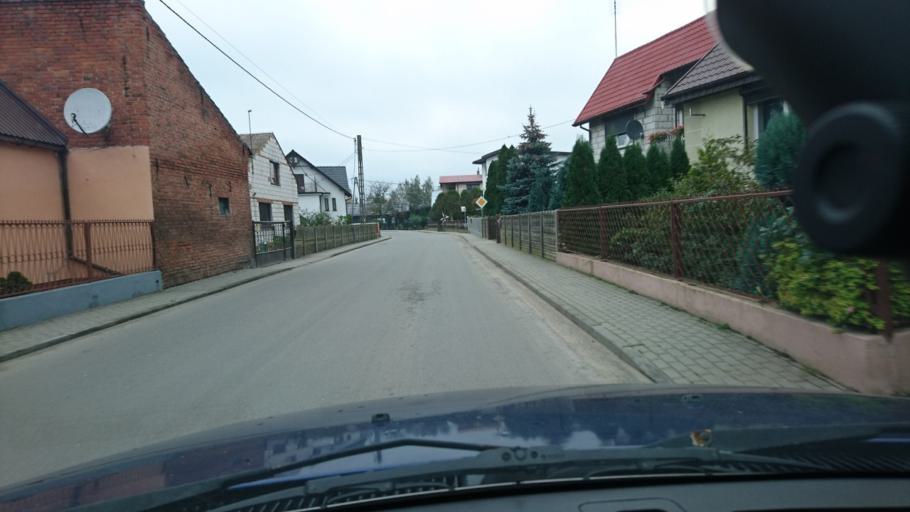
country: PL
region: Greater Poland Voivodeship
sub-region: Powiat krotoszynski
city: Sulmierzyce
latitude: 51.5671
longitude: 17.5889
